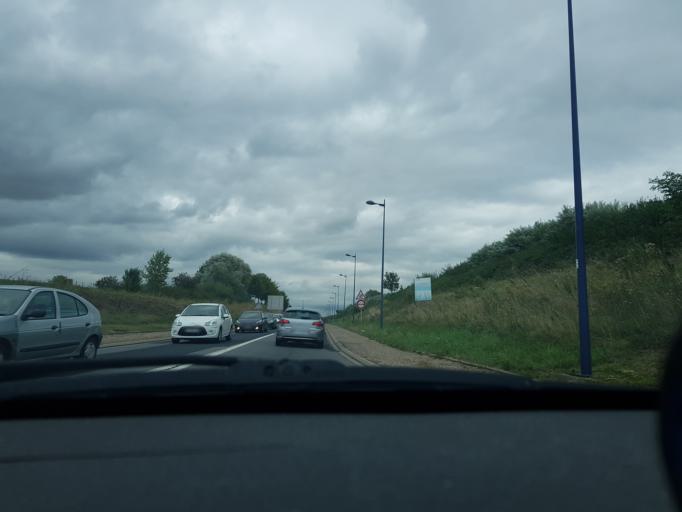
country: FR
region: Lorraine
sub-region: Departement de Meurthe-et-Moselle
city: Saulxures-les-Nancy
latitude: 48.6860
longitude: 6.2312
